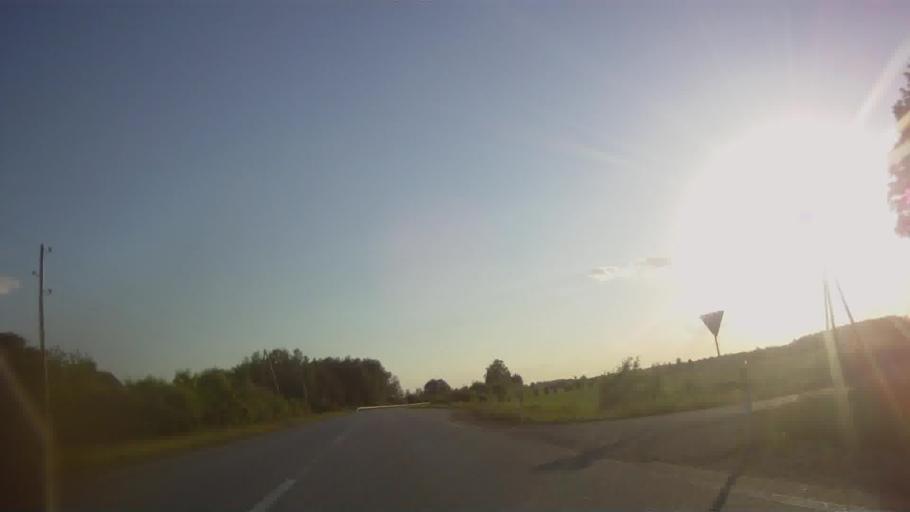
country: LV
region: Livani
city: Livani
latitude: 56.5344
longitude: 26.2973
